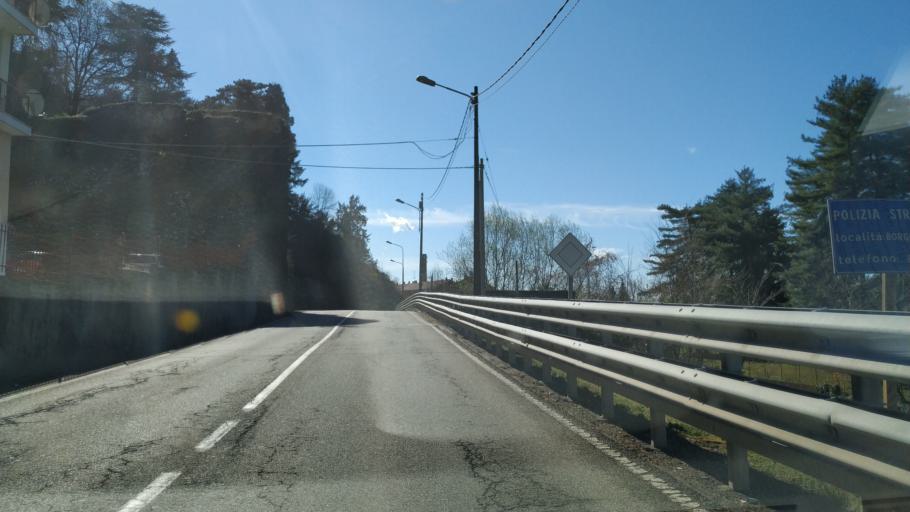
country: IT
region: Piedmont
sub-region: Provincia di Novara
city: Romagnano Sesia
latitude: 45.6375
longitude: 8.3781
